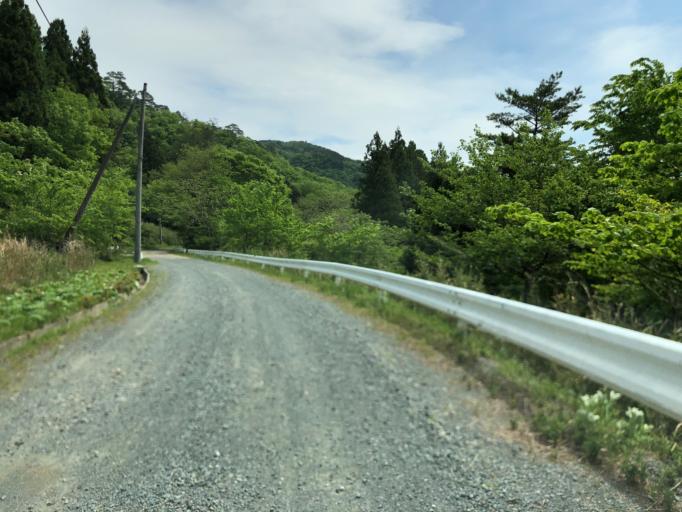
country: JP
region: Miyagi
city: Marumori
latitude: 37.7327
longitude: 140.8316
